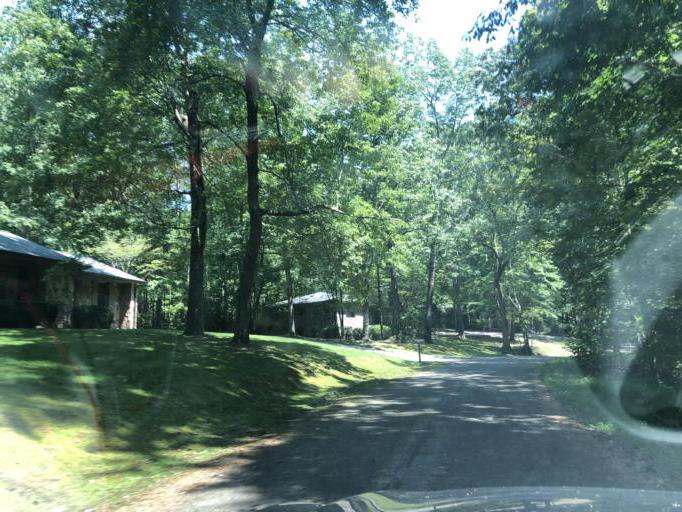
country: US
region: Tennessee
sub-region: Franklin County
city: Sewanee
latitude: 35.2035
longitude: -85.9292
